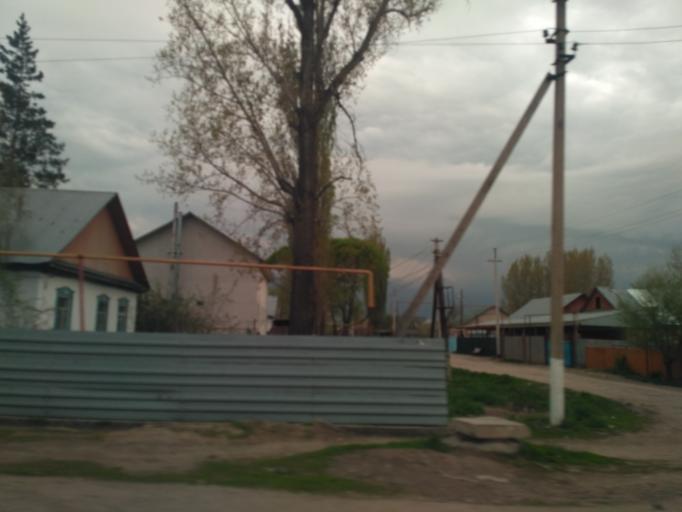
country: KZ
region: Almaty Oblysy
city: Burunday
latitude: 43.2109
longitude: 76.3227
